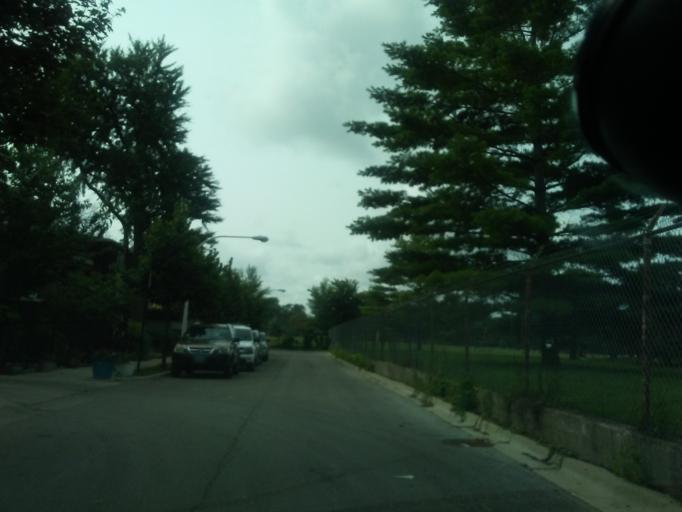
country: US
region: Illinois
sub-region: Cook County
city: Lincolnwood
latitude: 41.9939
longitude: -87.6849
